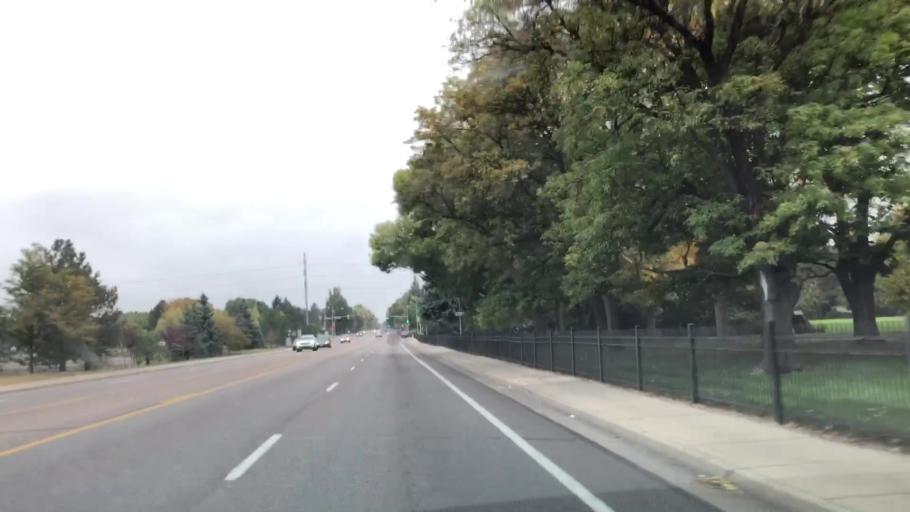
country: US
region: Colorado
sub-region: Larimer County
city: Fort Collins
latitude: 40.5543
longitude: -105.0581
